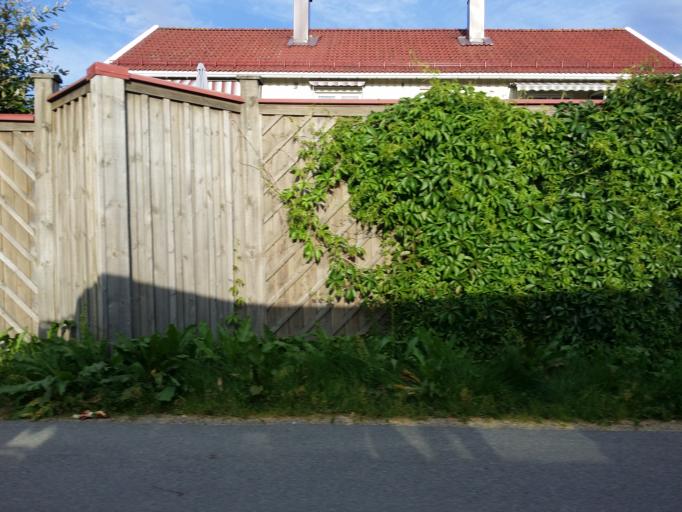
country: NO
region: Akershus
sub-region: Lorenskog
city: Kjenn
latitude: 59.9051
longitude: 10.8514
